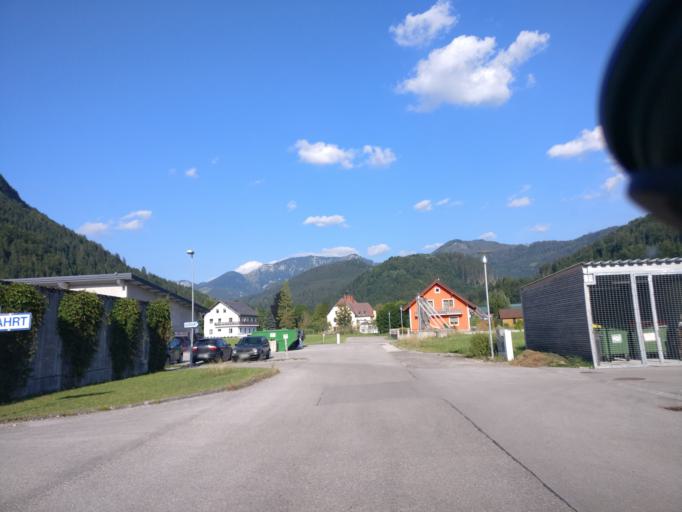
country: AT
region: Lower Austria
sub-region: Politischer Bezirk Scheibbs
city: Gostling an der Ybbs
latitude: 47.8067
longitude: 14.9387
